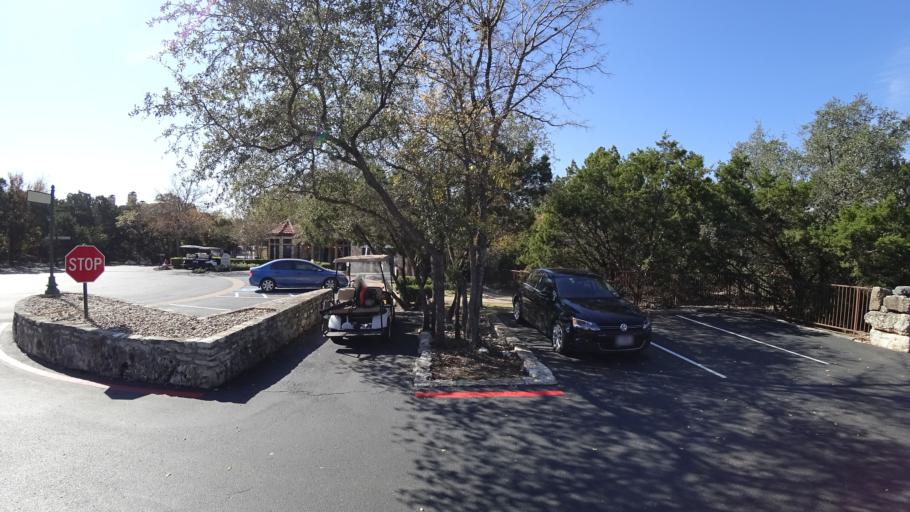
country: US
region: Texas
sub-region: Williamson County
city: Jollyville
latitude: 30.3724
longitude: -97.7615
